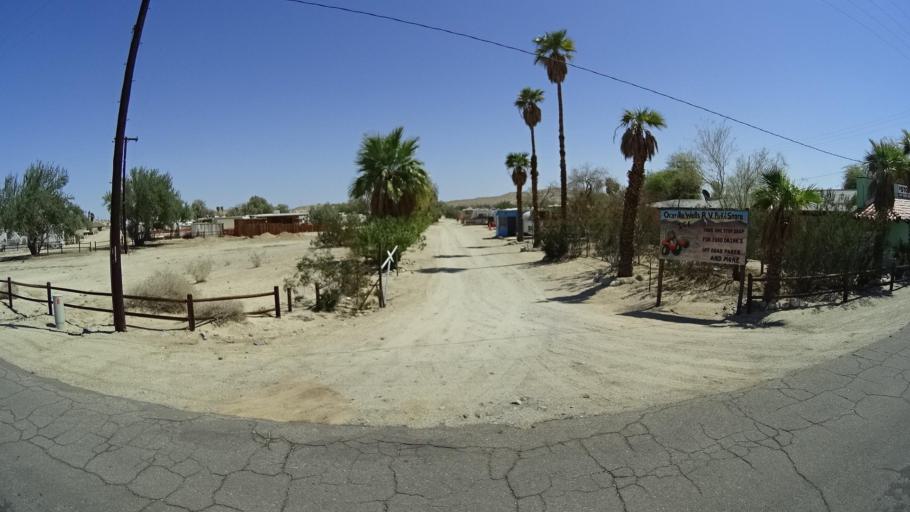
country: US
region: California
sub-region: Imperial County
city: Salton City
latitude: 33.1366
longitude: -116.1328
